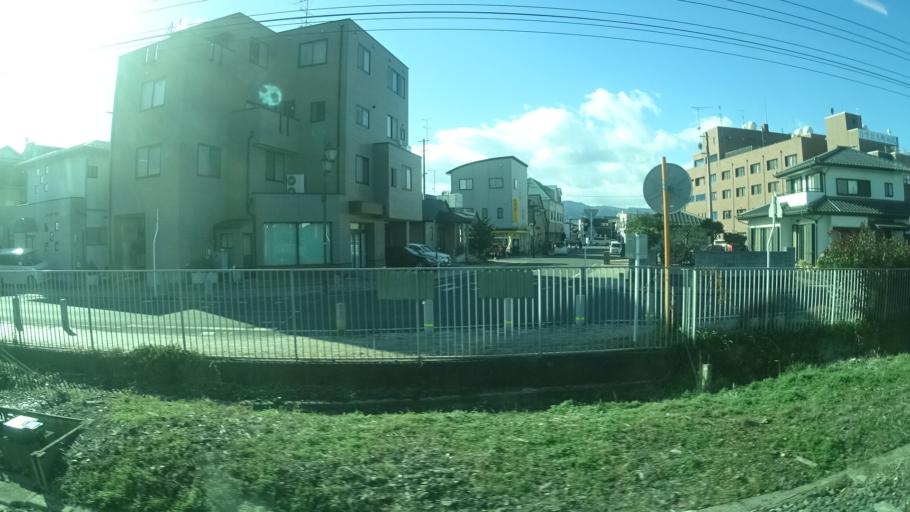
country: JP
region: Fukushima
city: Namie
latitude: 37.6400
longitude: 140.9691
